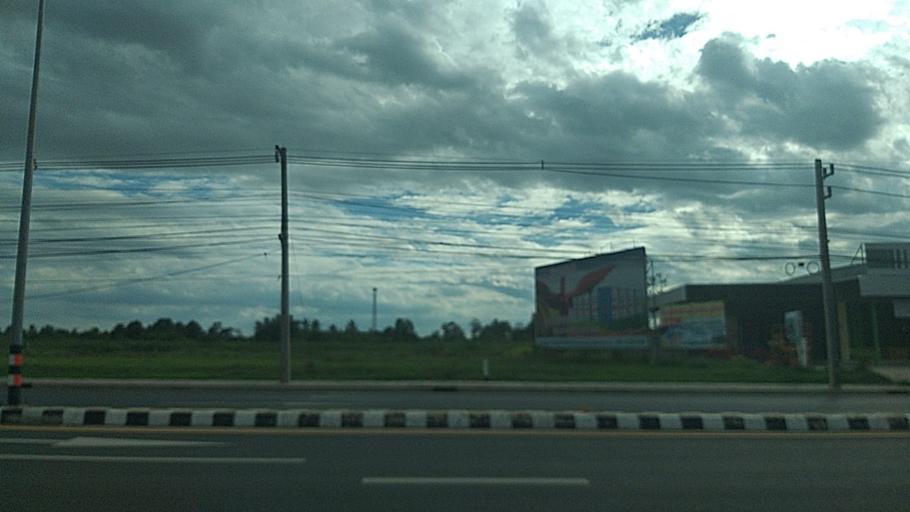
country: TH
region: Surin
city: Prasat
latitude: 14.6270
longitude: 103.4100
